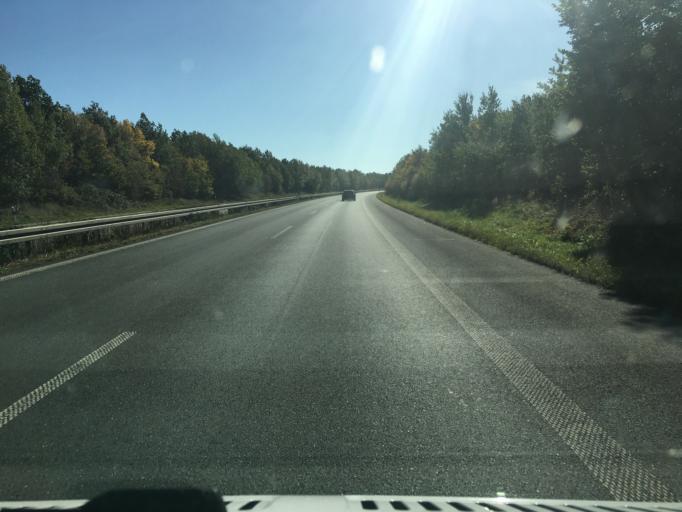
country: DE
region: Saxony
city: Dennheritz
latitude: 50.8079
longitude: 12.4536
